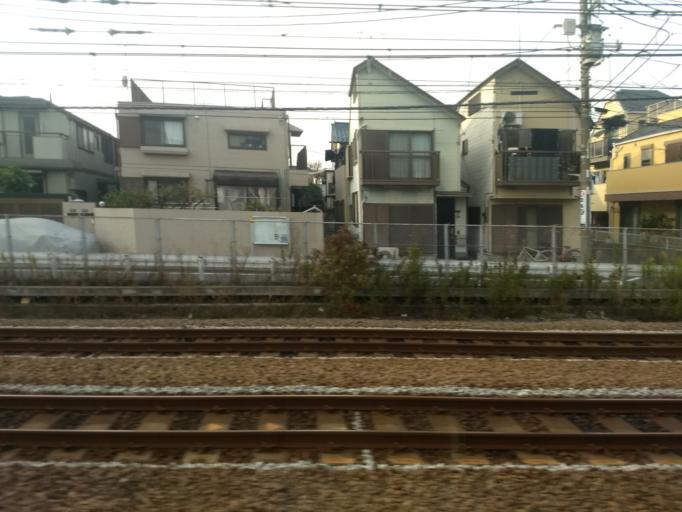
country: JP
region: Kanagawa
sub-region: Kawasaki-shi
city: Kawasaki
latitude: 35.5953
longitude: 139.7322
